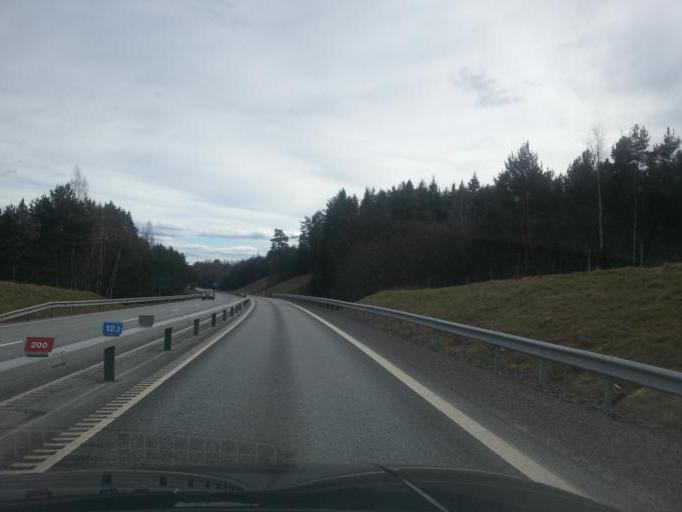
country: SE
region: Joenkoeping
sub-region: Jonkopings Kommun
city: Bankeryd
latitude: 57.8723
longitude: 14.1016
